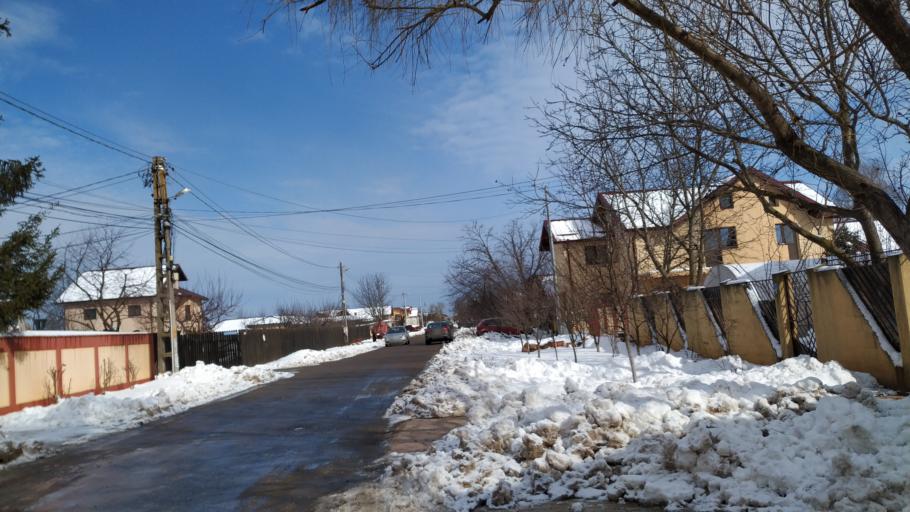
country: RO
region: Ilfov
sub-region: Comuna Berceni
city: Berceni
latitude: 44.3187
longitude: 26.1907
